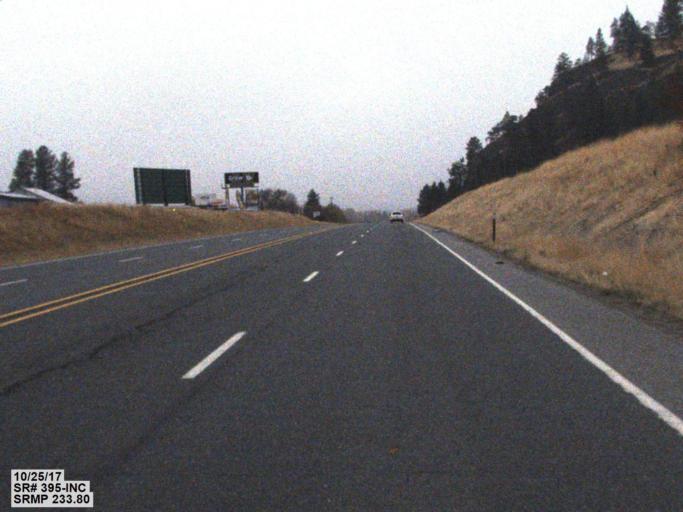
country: US
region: Washington
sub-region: Stevens County
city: Colville
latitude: 48.5851
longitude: -117.9715
